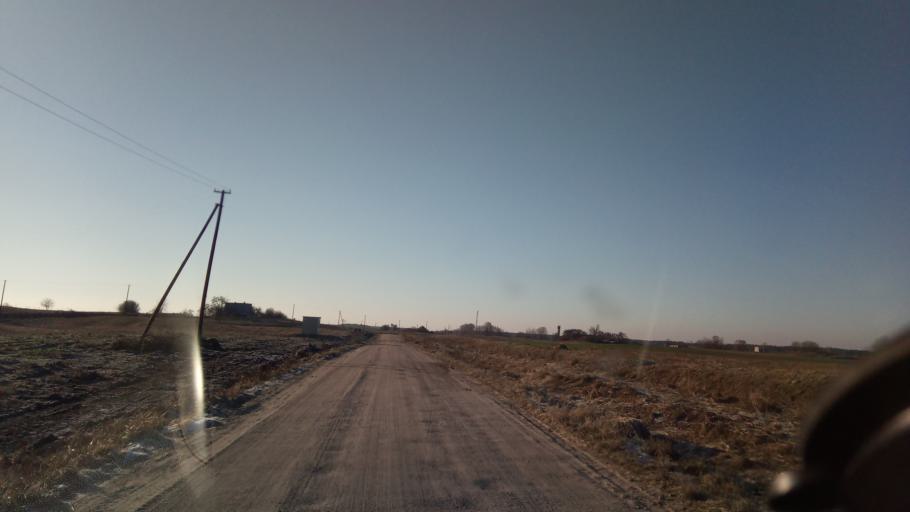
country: LT
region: Alytaus apskritis
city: Druskininkai
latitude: 54.0900
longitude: 23.9916
